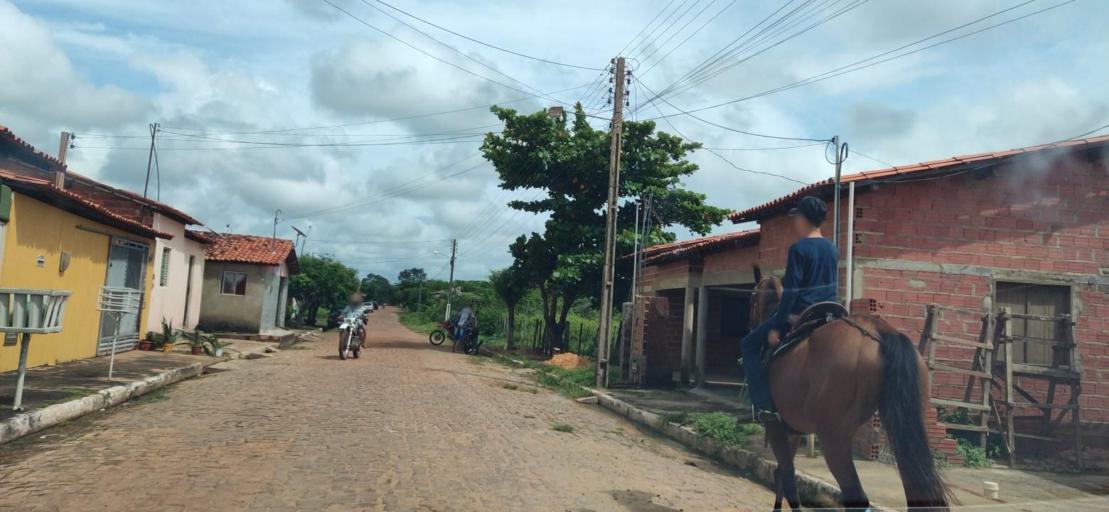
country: BR
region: Piaui
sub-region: Valenca Do Piaui
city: Valenca do Piaui
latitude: -6.1107
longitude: -41.7975
